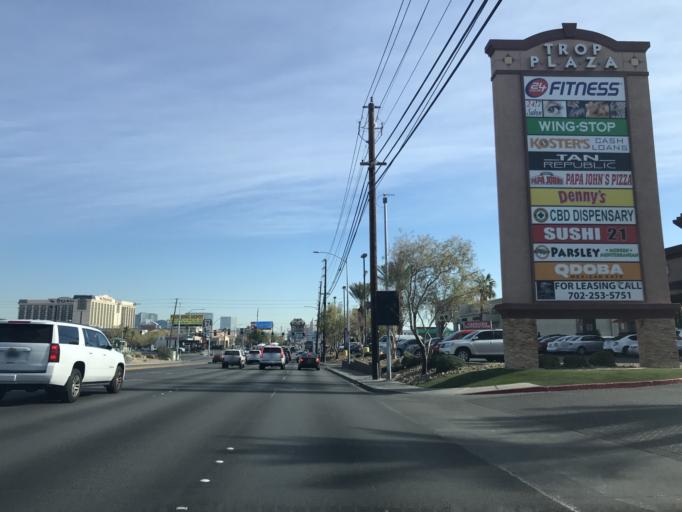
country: US
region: Nevada
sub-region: Clark County
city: Spring Valley
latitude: 36.1007
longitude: -115.2101
